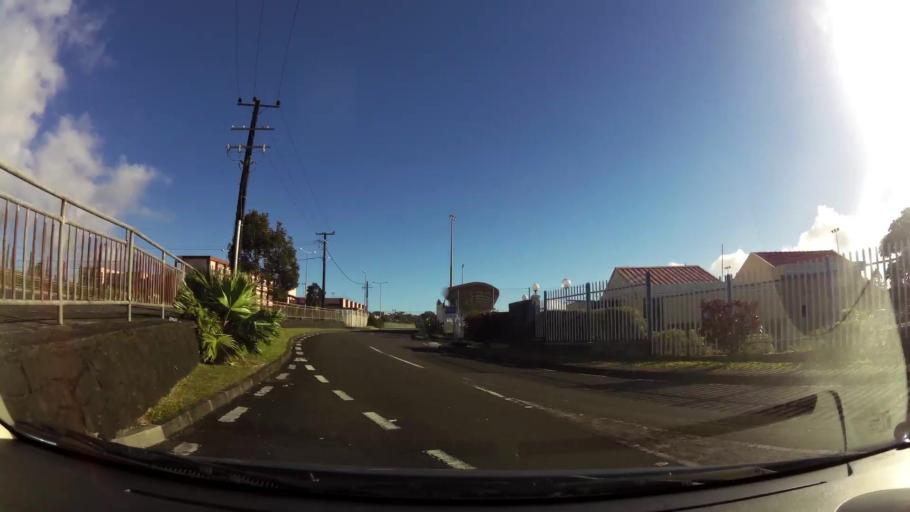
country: MU
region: Plaines Wilhems
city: Curepipe
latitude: -20.3228
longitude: 57.5387
